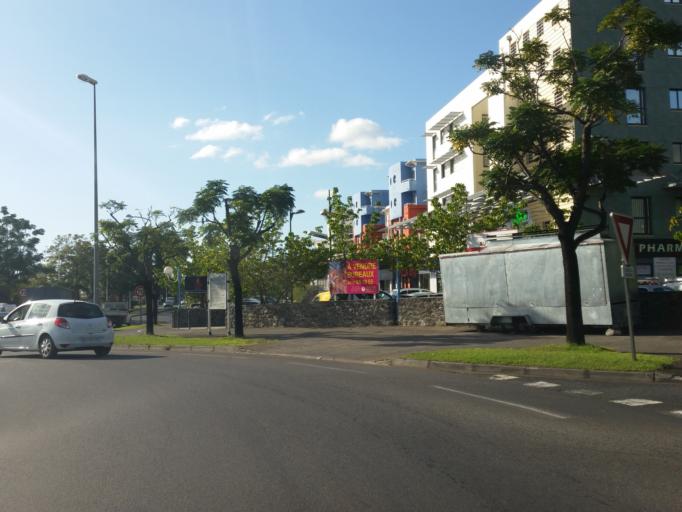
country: RE
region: Reunion
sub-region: Reunion
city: Saint-Denis
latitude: -20.8998
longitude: 55.4797
